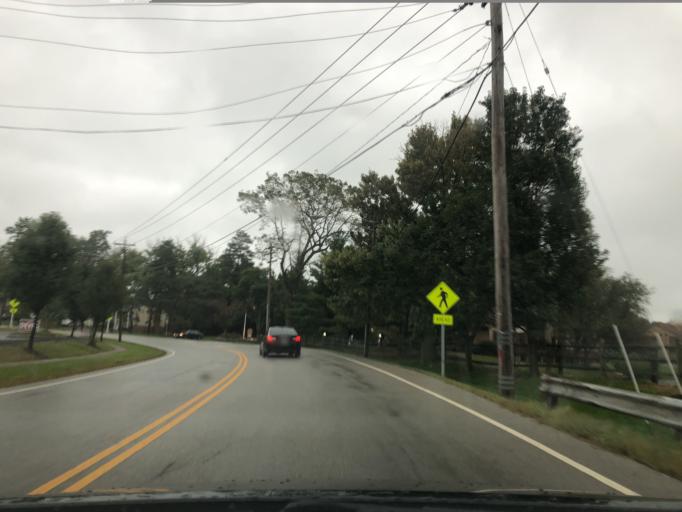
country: US
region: Ohio
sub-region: Hamilton County
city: Dillonvale
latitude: 39.2275
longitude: -84.3918
